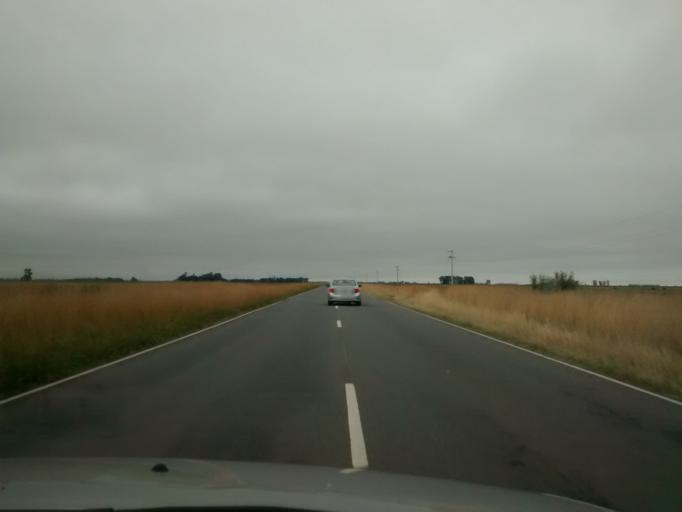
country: AR
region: Buenos Aires
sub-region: Partido de Ayacucho
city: Ayacucho
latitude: -37.0307
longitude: -58.5397
